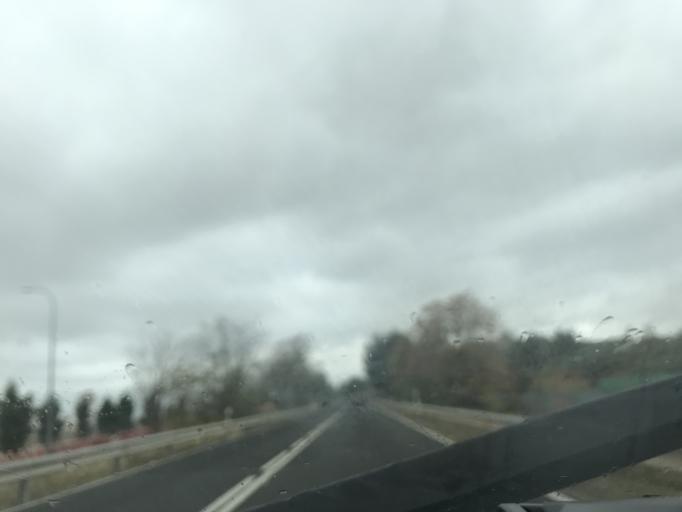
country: ES
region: Andalusia
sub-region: Provincia de Jaen
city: Peal de Becerro
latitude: 37.9160
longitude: -3.1066
